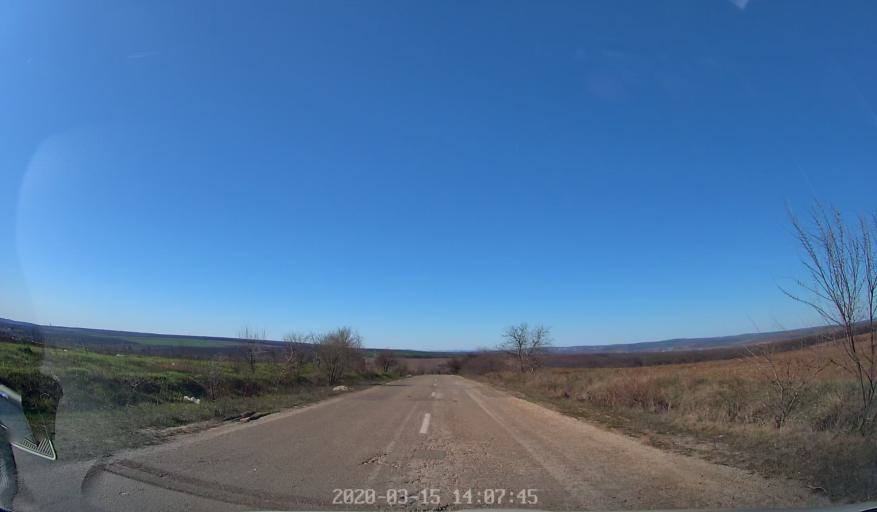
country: MD
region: Orhei
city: Orhei
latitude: 47.3046
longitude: 28.9452
